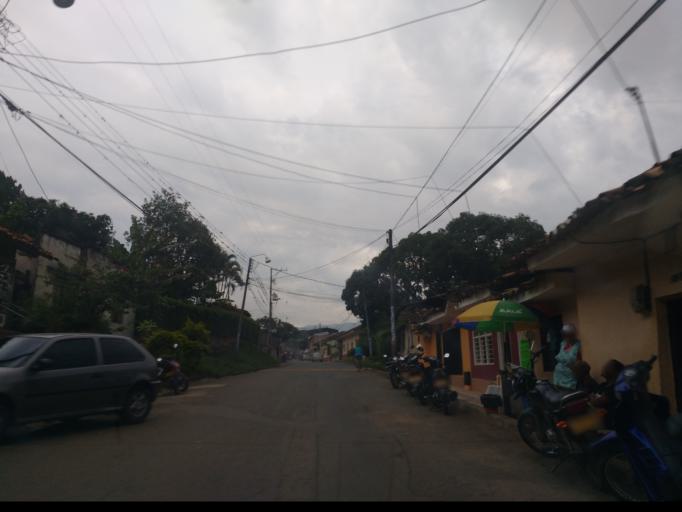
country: CO
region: Cauca
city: Santander de Quilichao
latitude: 3.0025
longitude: -76.4780
